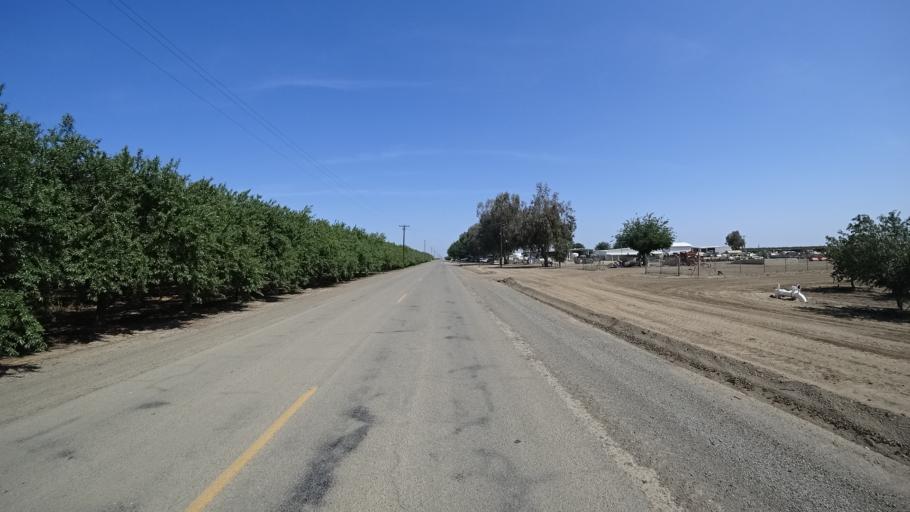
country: US
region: California
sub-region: Kings County
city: Kettleman City
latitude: 36.0909
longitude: -120.0037
